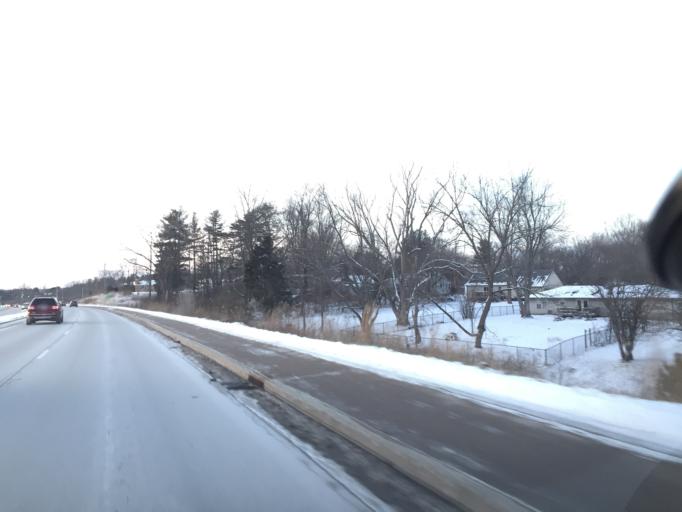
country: US
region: Indiana
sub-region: Monroe County
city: Bloomington
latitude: 39.1850
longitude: -86.5155
